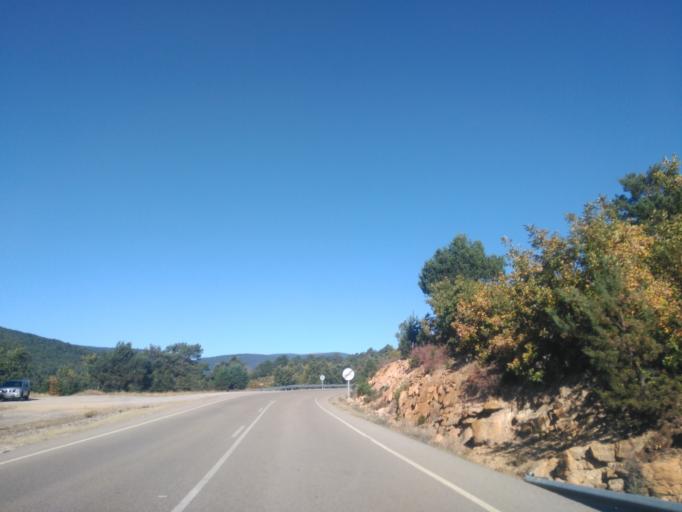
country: ES
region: Castille and Leon
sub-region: Provincia de Soria
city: Vinuesa
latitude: 41.8836
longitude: -2.7211
